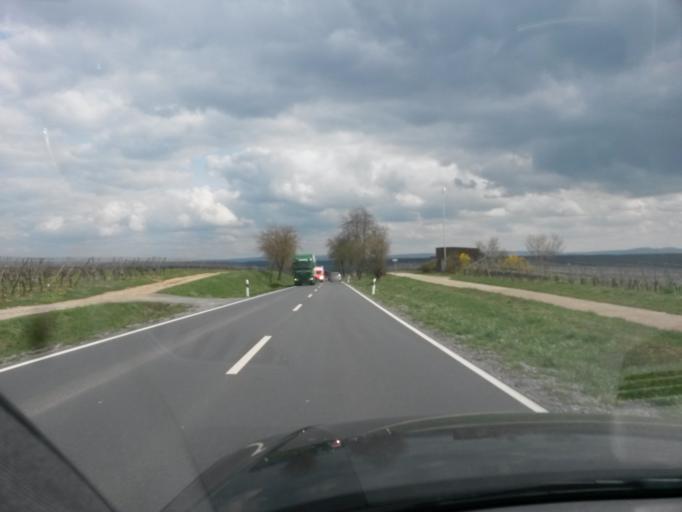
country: DE
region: Bavaria
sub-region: Regierungsbezirk Unterfranken
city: Nordheim
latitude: 49.8664
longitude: 10.1988
